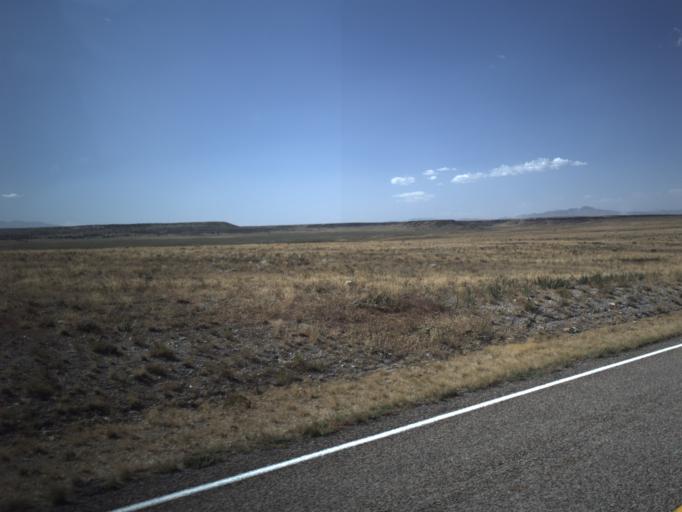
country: US
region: Utah
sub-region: Beaver County
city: Milford
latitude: 38.8030
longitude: -112.8866
